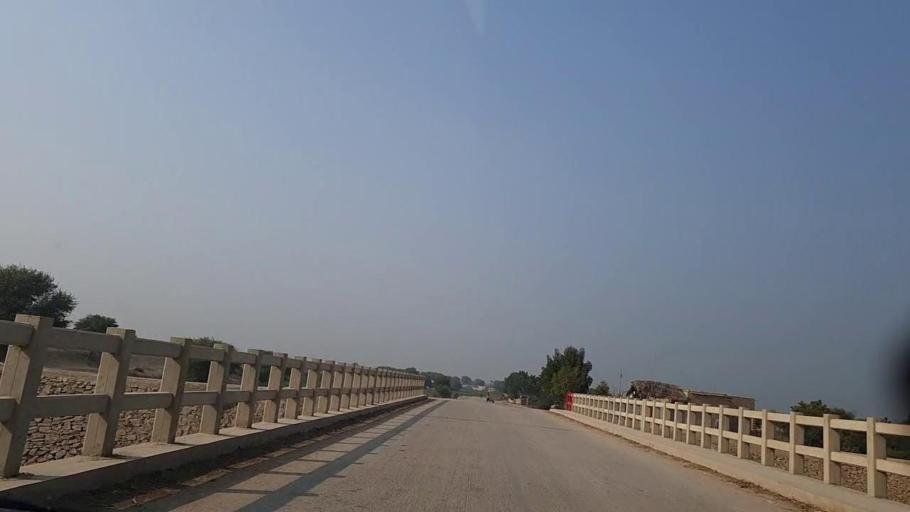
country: PK
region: Sindh
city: Sann
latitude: 26.1683
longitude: 68.1092
